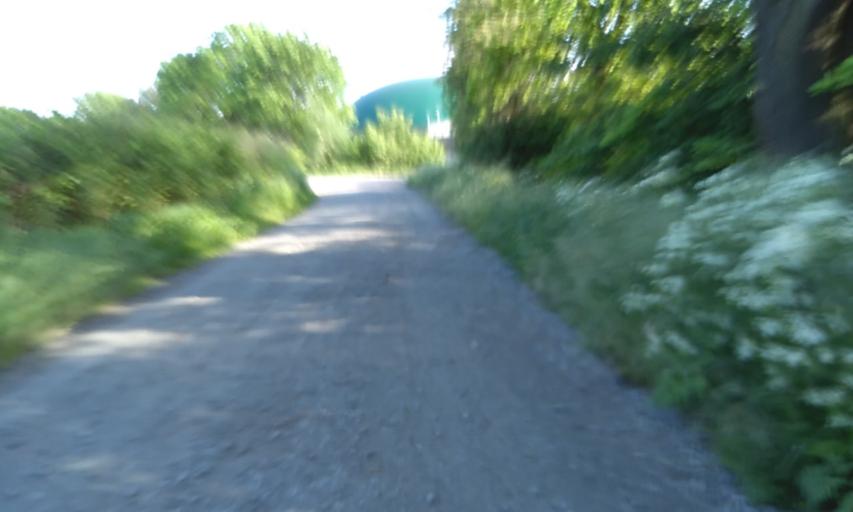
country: DE
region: Lower Saxony
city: Dollern
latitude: 53.5433
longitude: 9.5360
